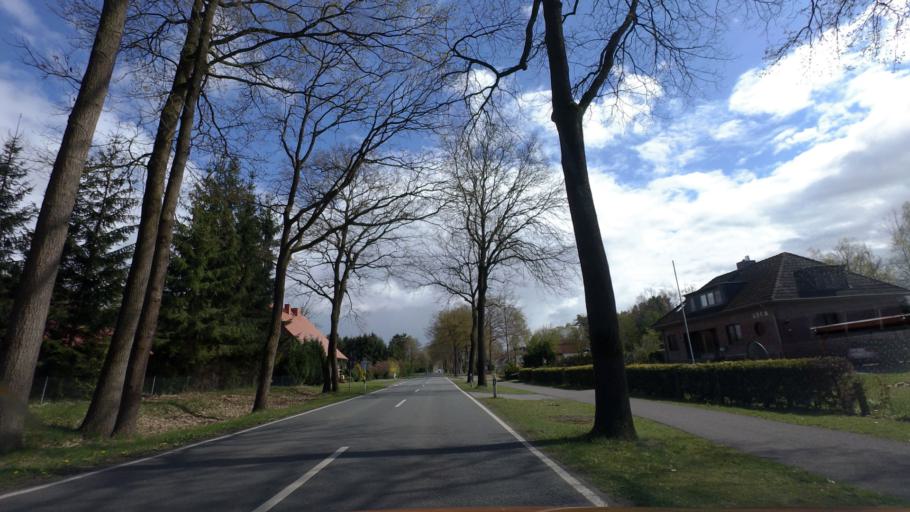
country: DE
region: Lower Saxony
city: Schneverdingen
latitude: 53.1161
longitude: 9.7589
